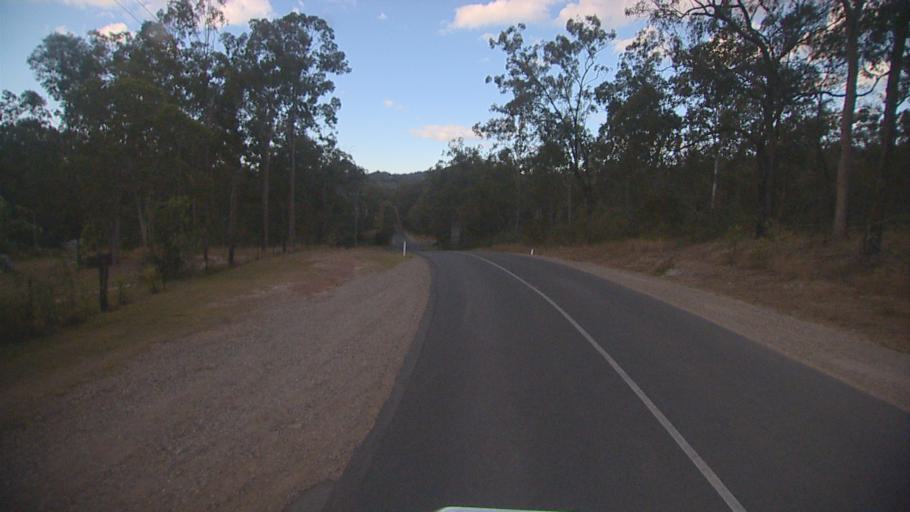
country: AU
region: Queensland
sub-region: Logan
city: Windaroo
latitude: -27.8150
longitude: 153.1658
